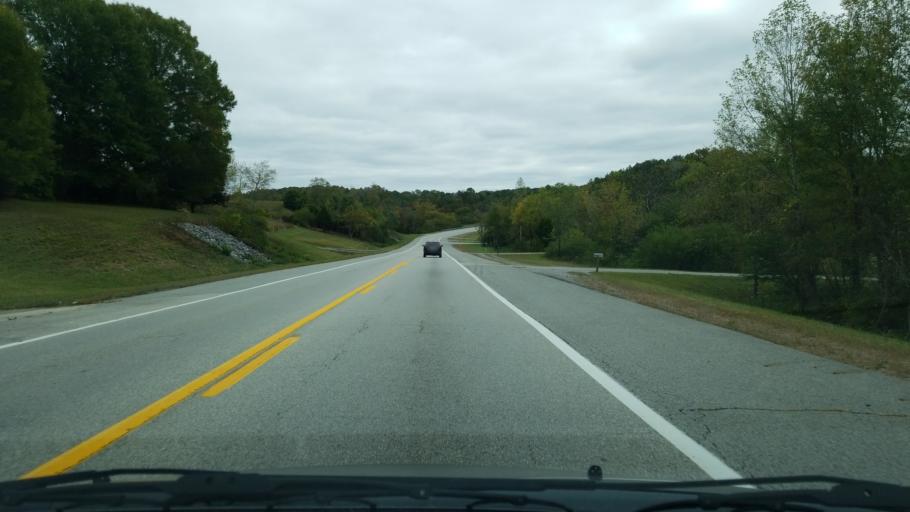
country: US
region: Tennessee
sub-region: Rhea County
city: Dayton
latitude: 35.4590
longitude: -85.0129
